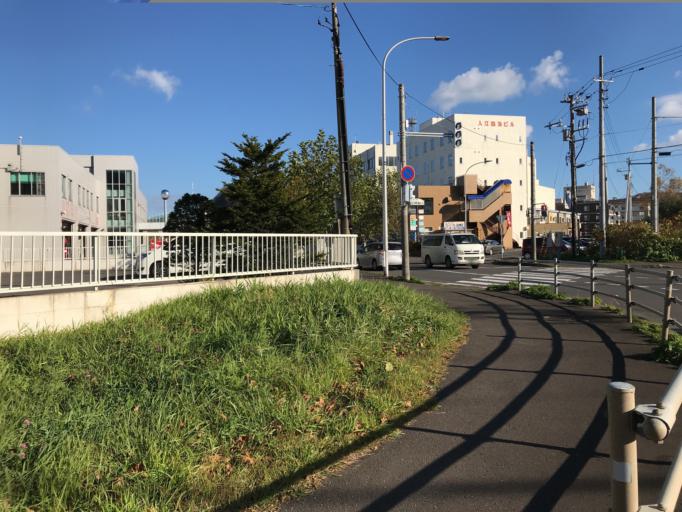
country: JP
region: Hokkaido
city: Muroran
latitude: 42.3230
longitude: 140.9705
